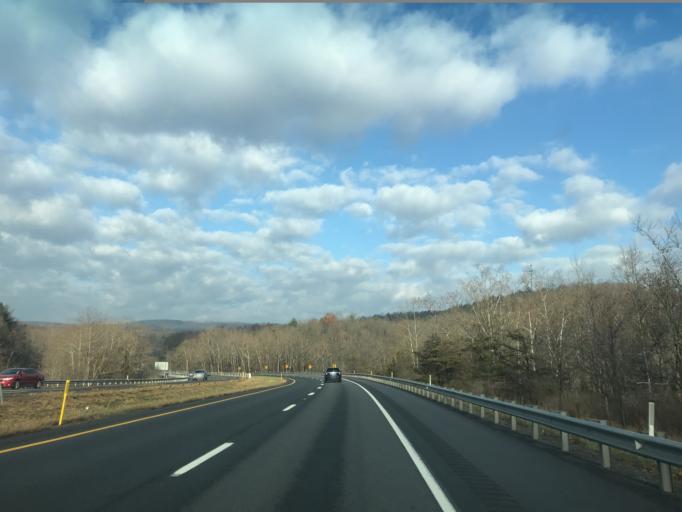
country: US
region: Maryland
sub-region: Washington County
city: Hancock
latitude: 39.7800
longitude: -78.2032
